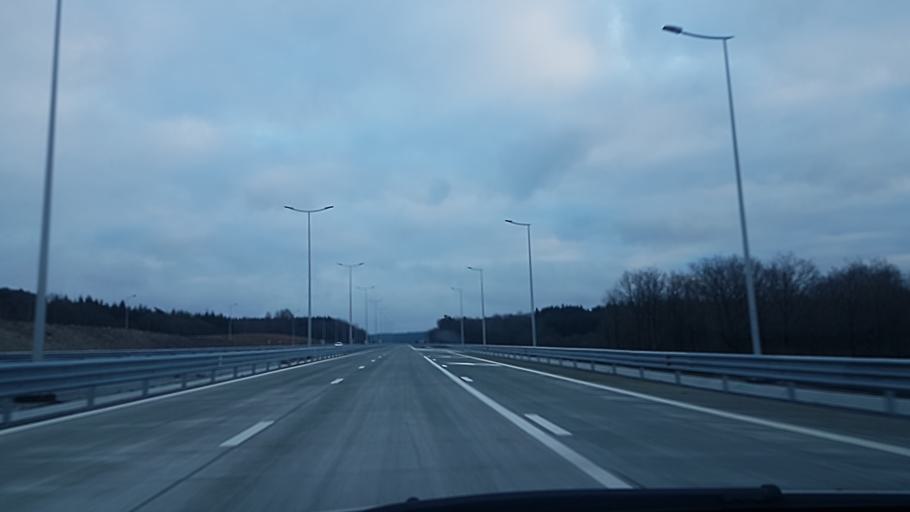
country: BE
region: Wallonia
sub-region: Province de Namur
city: Couvin
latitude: 50.0231
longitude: 4.5230
